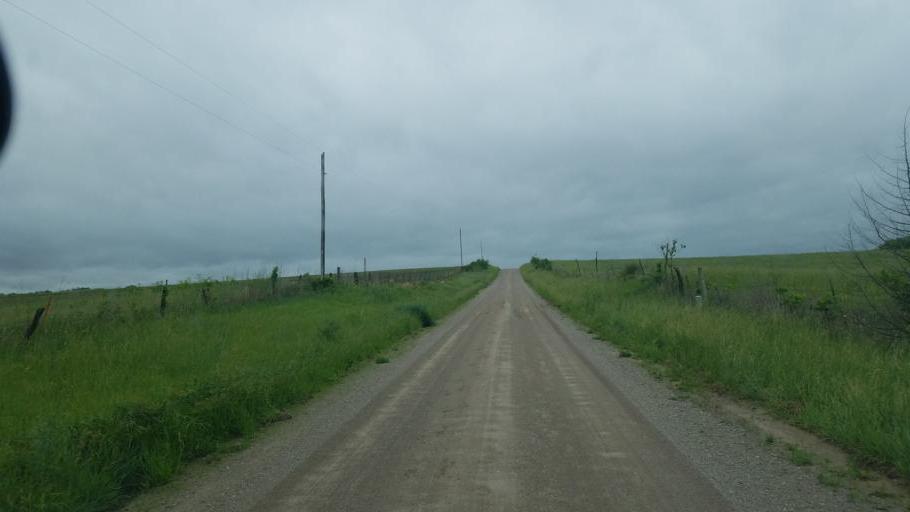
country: US
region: Missouri
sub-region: Carroll County
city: Carrollton
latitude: 39.4852
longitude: -93.4975
